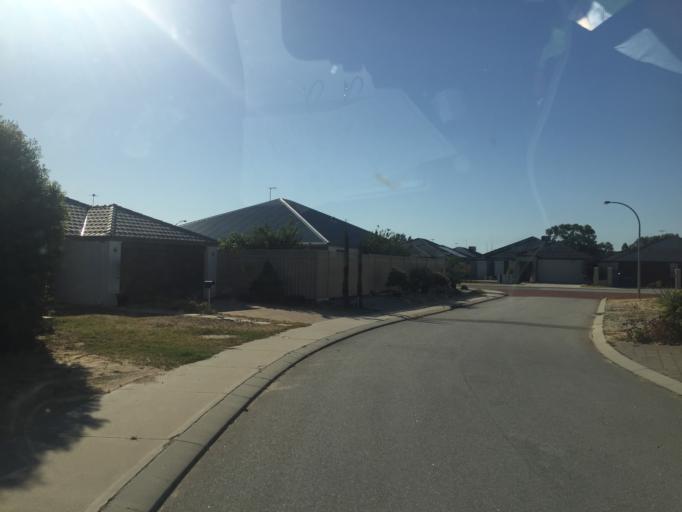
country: AU
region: Western Australia
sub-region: Canning
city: East Cannington
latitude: -32.0035
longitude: 115.9792
